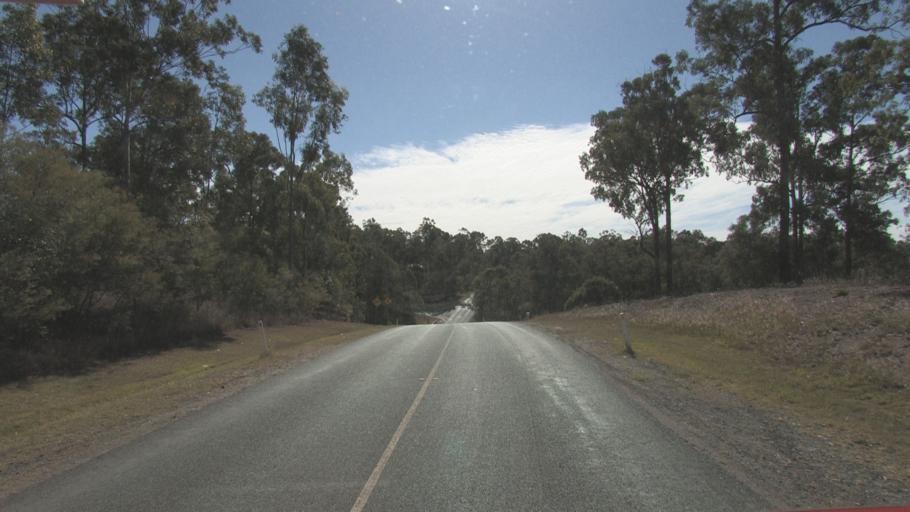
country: AU
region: Queensland
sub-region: Ipswich
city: Springfield Lakes
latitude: -27.7157
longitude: 152.9163
